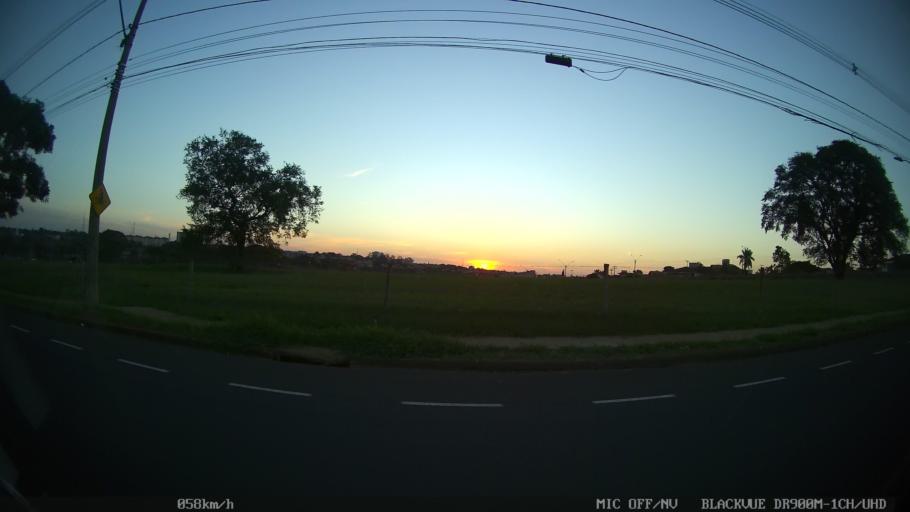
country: BR
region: Sao Paulo
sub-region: Sao Jose Do Rio Preto
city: Sao Jose do Rio Preto
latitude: -20.8228
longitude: -49.3411
